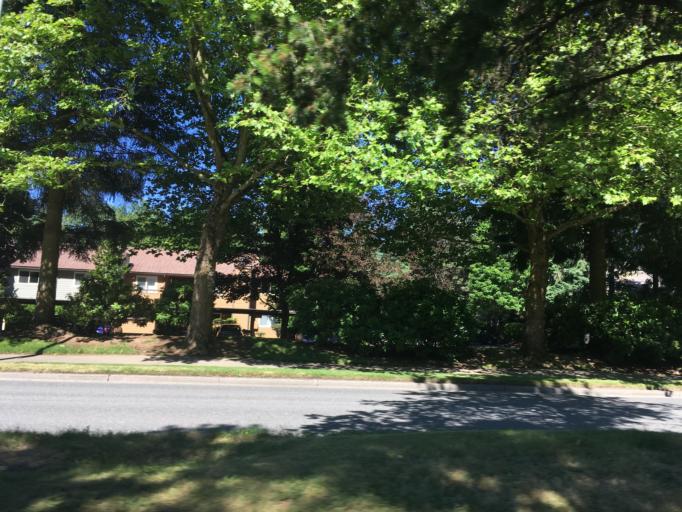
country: US
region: Washington
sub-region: King County
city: Redmond
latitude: 47.6540
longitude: -122.1433
